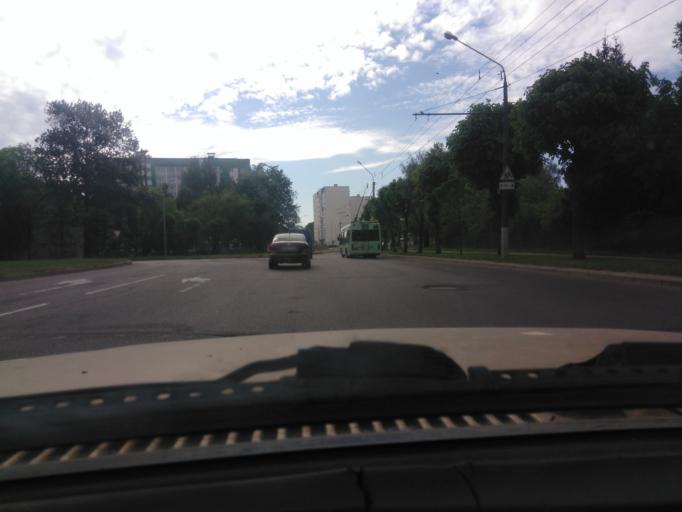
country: BY
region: Mogilev
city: Buynichy
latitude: 53.8976
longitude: 30.2944
